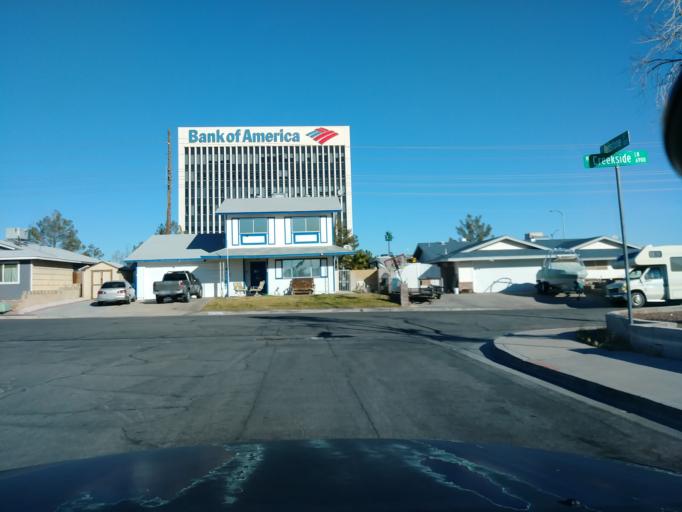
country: US
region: Nevada
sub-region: Clark County
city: Spring Valley
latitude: 36.1732
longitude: -115.2469
